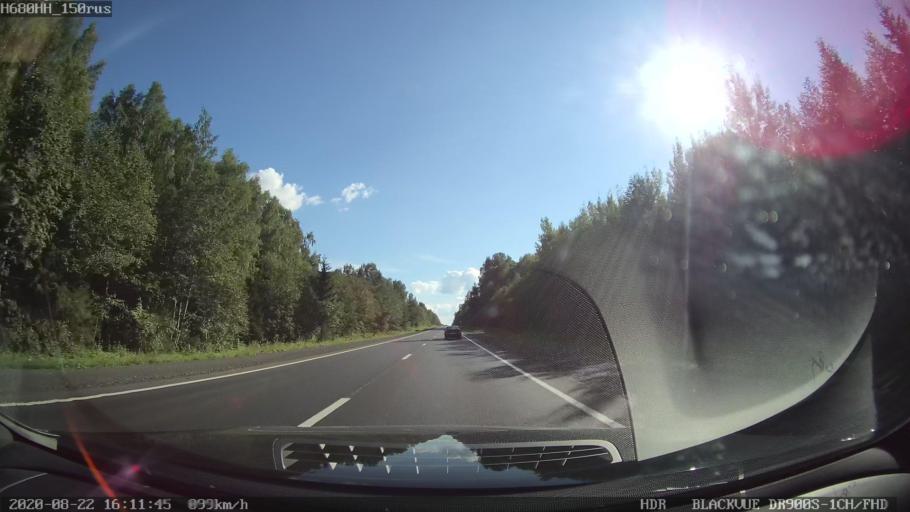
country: RU
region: Tverskaya
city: Rameshki
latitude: 57.4977
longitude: 36.2568
